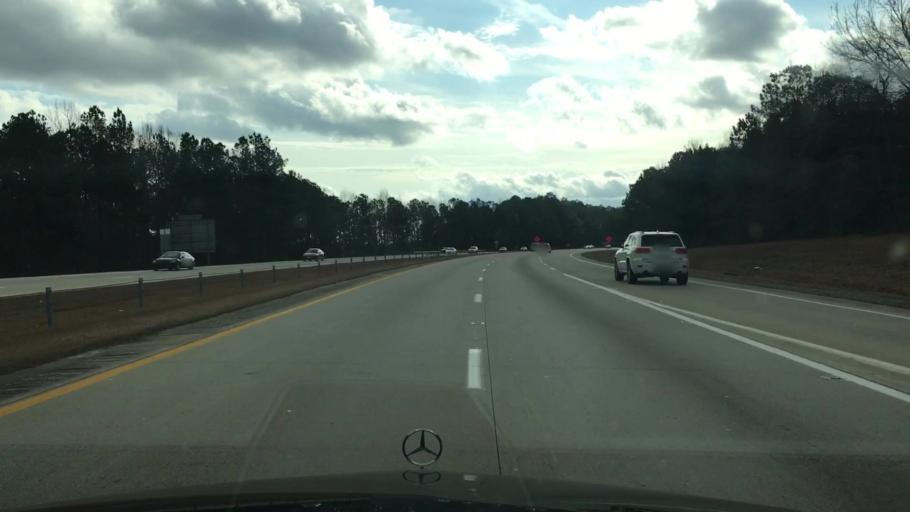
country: US
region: North Carolina
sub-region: Johnston County
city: Clayton
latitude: 35.6029
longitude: -78.5635
